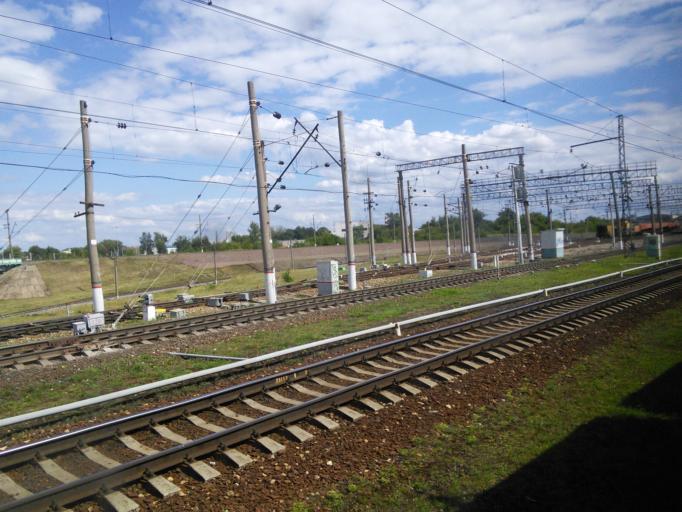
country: RU
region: Moscow
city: Nekrasovka
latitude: 55.6711
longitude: 37.9187
